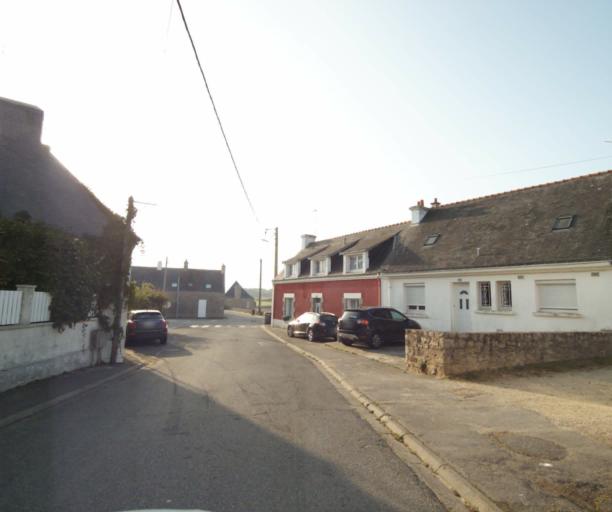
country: FR
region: Brittany
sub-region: Departement du Morbihan
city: Riantec
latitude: 47.7092
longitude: -3.3277
